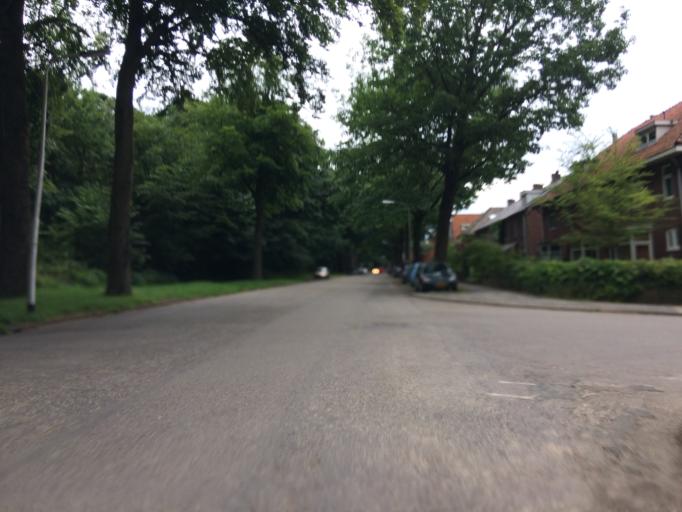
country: NL
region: Gelderland
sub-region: Gemeente Nijmegen
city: Nijmegen
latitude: 51.8142
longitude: 5.8705
